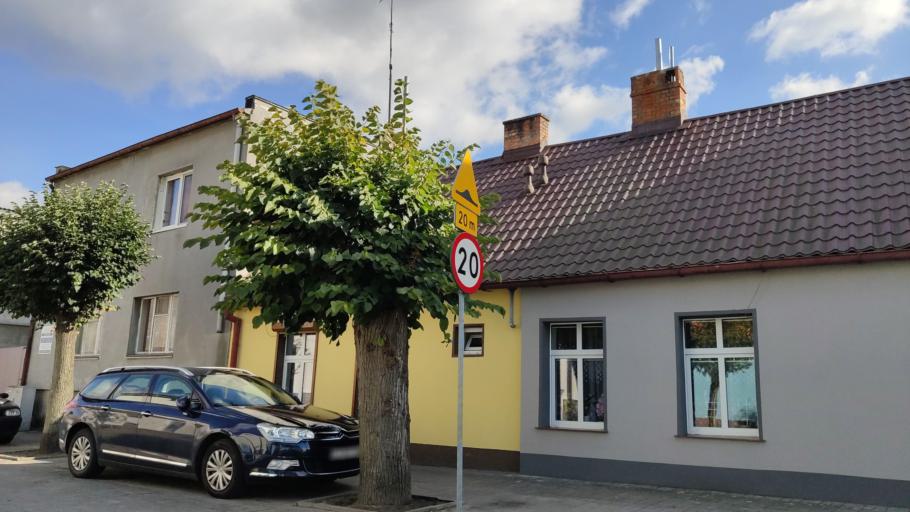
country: PL
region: Kujawsko-Pomorskie
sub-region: Powiat zninski
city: Barcin
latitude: 52.8642
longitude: 17.9428
